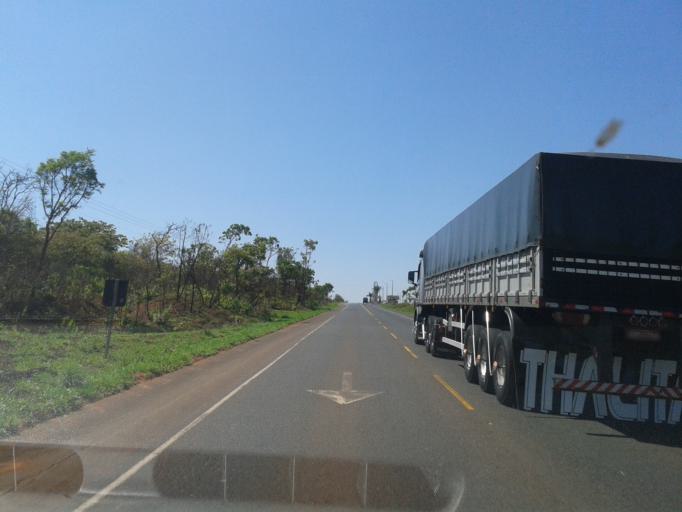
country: BR
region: Minas Gerais
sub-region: Uberlandia
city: Uberlandia
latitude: -19.0975
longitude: -47.9923
